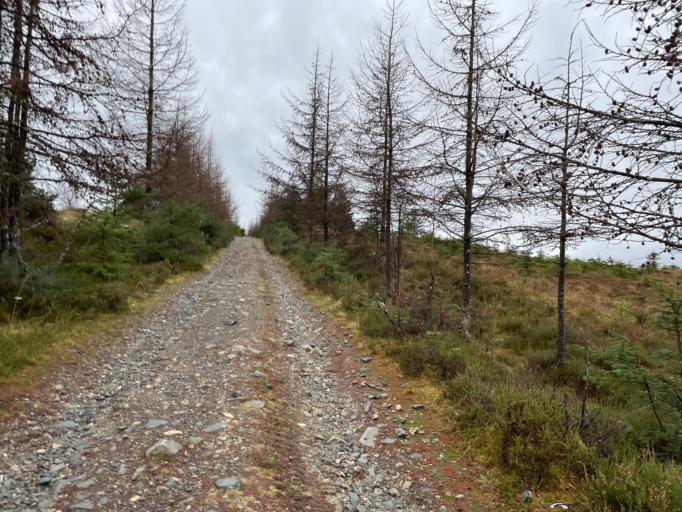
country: GB
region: Scotland
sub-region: Highland
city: Fort William
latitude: 56.8119
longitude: -5.0941
